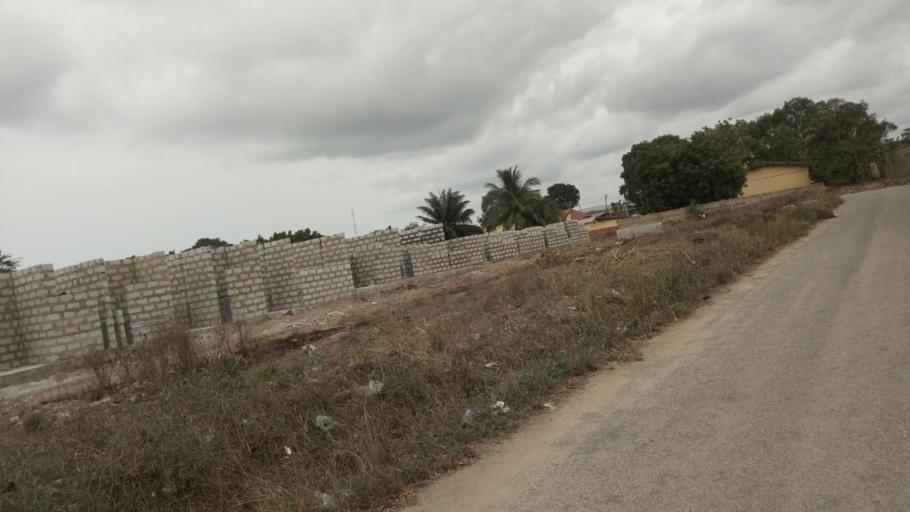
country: GH
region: Central
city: Winneba
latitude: 5.3815
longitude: -0.6399
